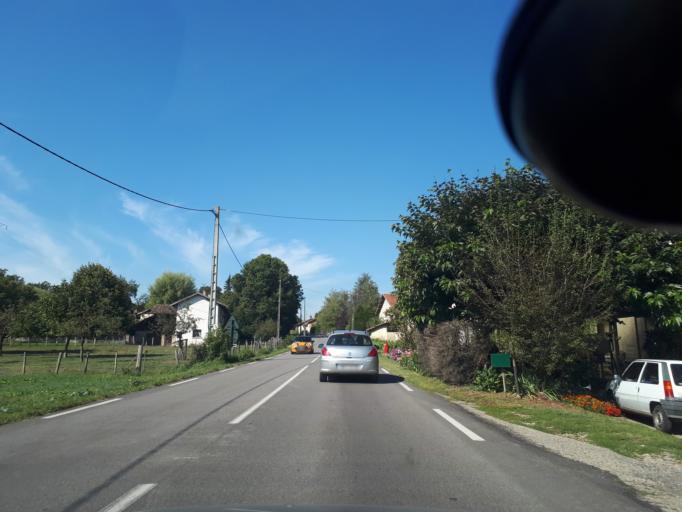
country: FR
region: Rhone-Alpes
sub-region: Departement de l'Isere
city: Maubec
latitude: 45.5489
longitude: 5.2592
